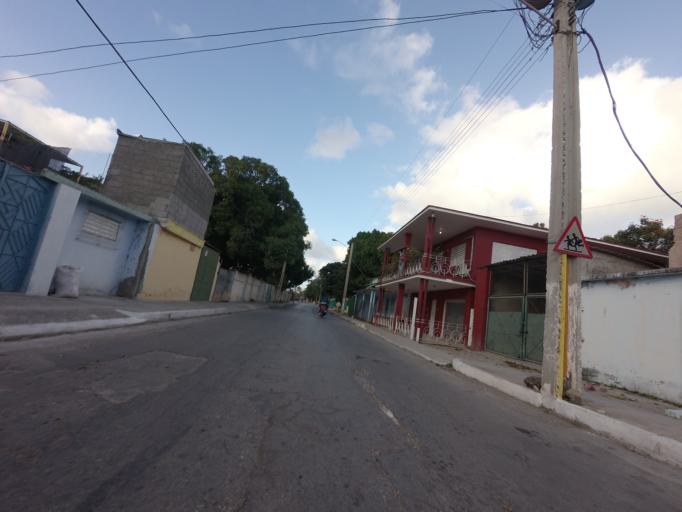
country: CU
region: Ciego de Avila
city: Ciego de Avila
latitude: 21.8386
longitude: -78.7553
